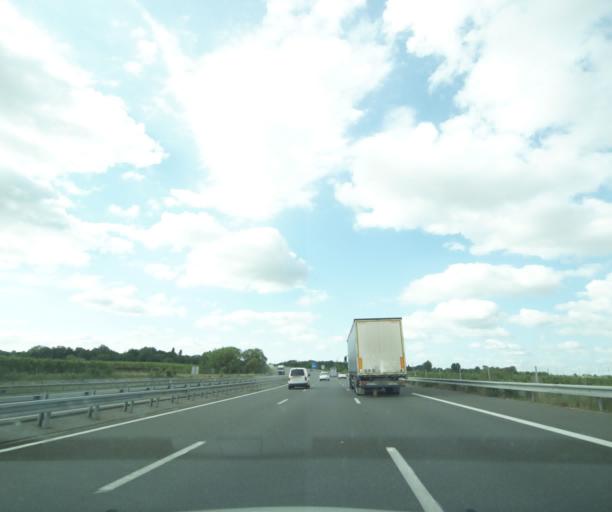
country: FR
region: Centre
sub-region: Departement du Loiret
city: Saint-Pryve-Saint-Mesmin
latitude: 47.8847
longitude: 1.8613
